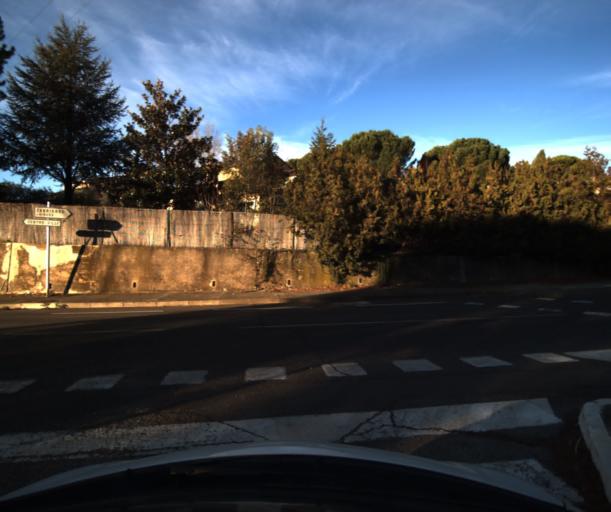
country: FR
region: Provence-Alpes-Cote d'Azur
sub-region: Departement du Vaucluse
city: Pertuis
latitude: 43.7033
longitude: 5.5056
